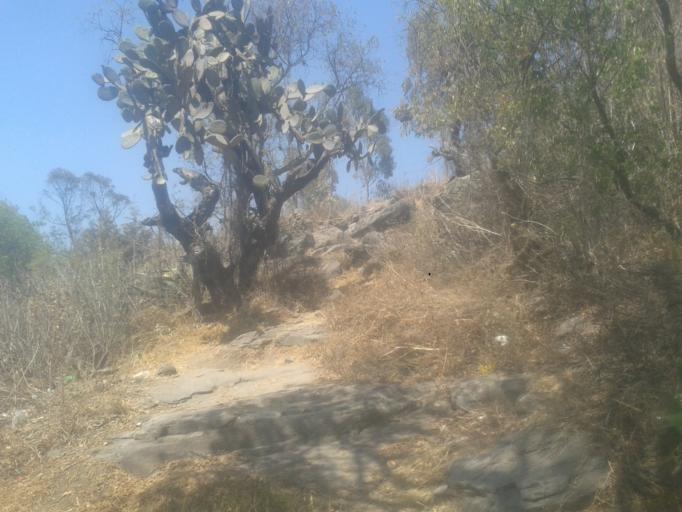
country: MX
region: Mexico
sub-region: Atlacomulco
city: San Bartolo Lanzados
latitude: 19.8954
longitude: -99.8588
